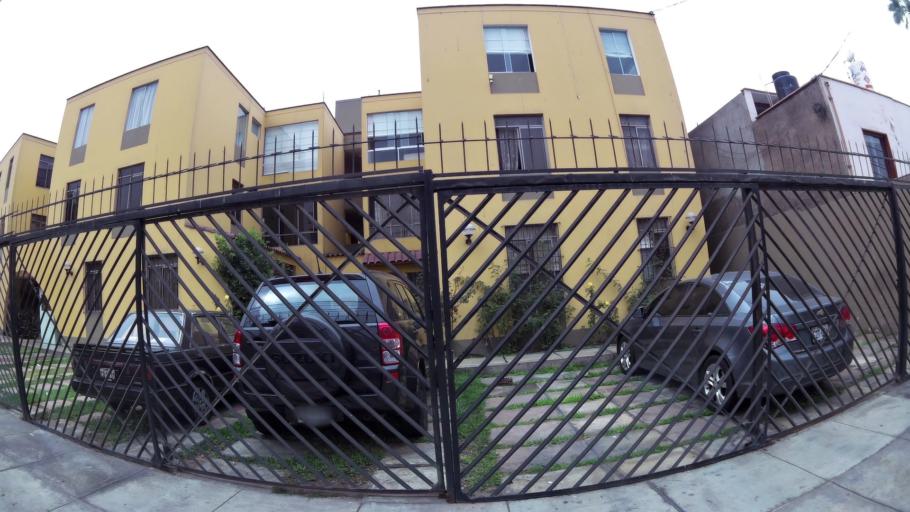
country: PE
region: Lima
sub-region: Lima
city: Surco
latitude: -12.1219
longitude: -77.0190
